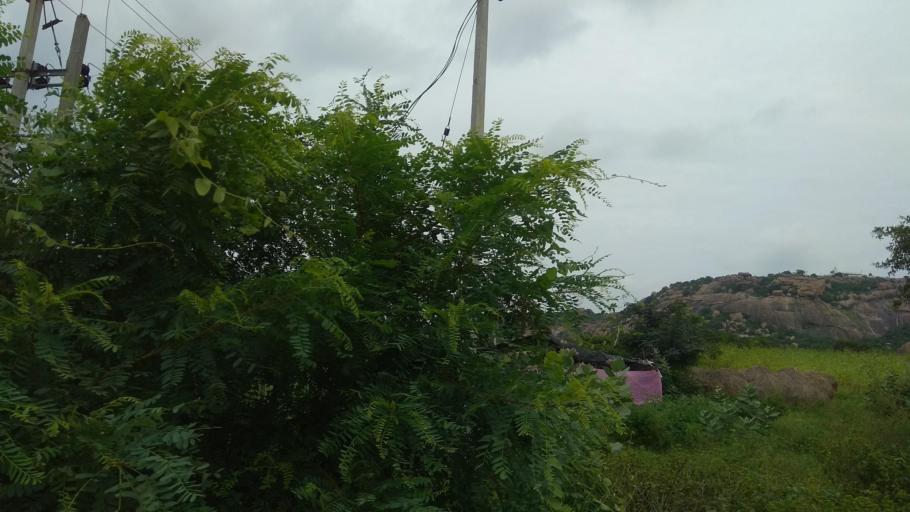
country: IN
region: Telangana
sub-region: Mahbubnagar
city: Farrukhnagar
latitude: 16.8830
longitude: 78.5010
